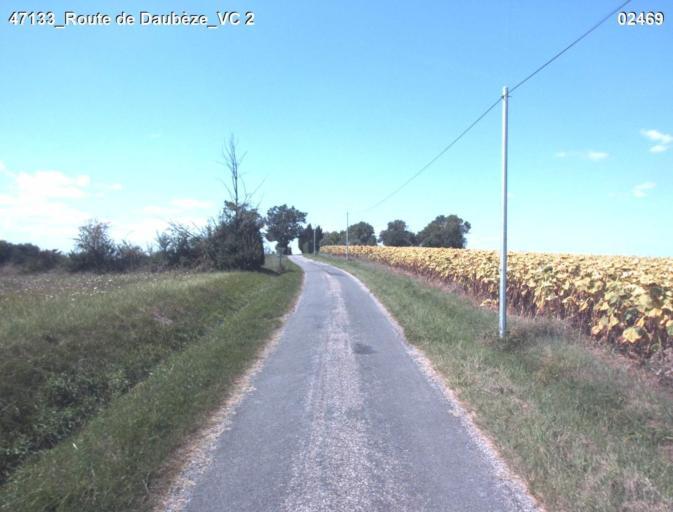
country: FR
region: Aquitaine
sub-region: Departement du Lot-et-Garonne
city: Laplume
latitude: 44.0779
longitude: 0.5620
